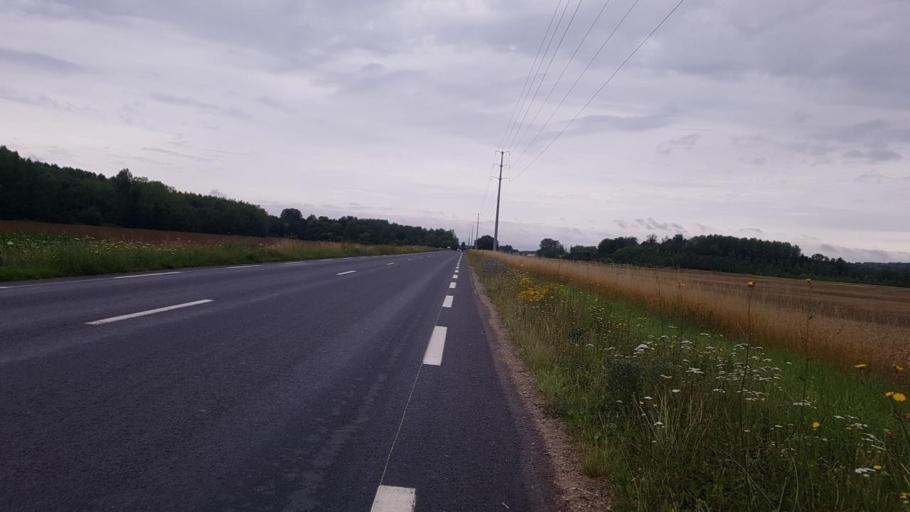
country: FR
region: Champagne-Ardenne
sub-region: Departement de la Marne
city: Vitry-le-Francois
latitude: 48.7410
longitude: 4.6554
